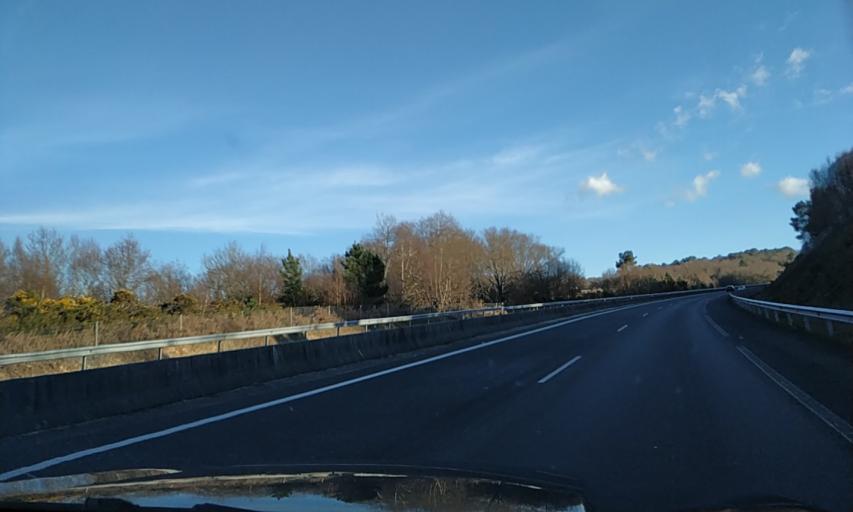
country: ES
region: Galicia
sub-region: Provincia de Pontevedra
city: Lalin
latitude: 42.6591
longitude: -8.1418
